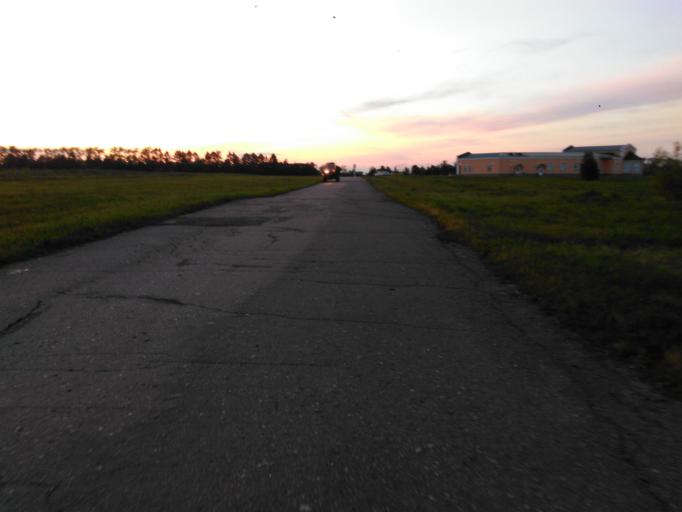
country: RU
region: Penza
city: Lermontovo
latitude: 52.9976
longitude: 43.6723
